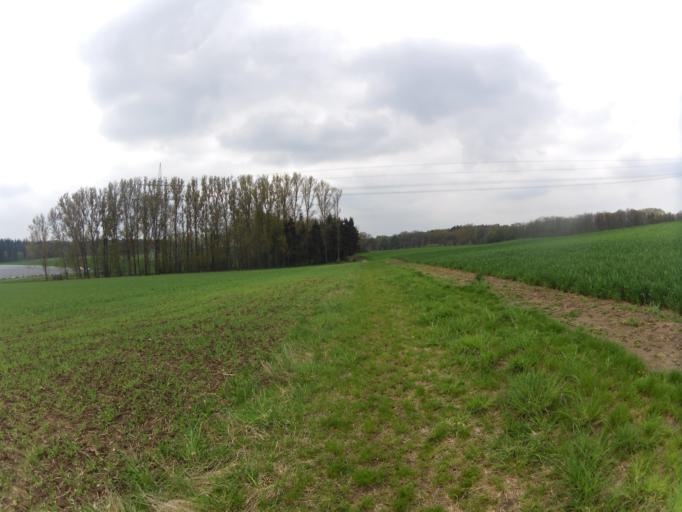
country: DE
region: Bavaria
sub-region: Regierungsbezirk Unterfranken
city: Frickenhausen
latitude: 49.7026
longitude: 10.0724
